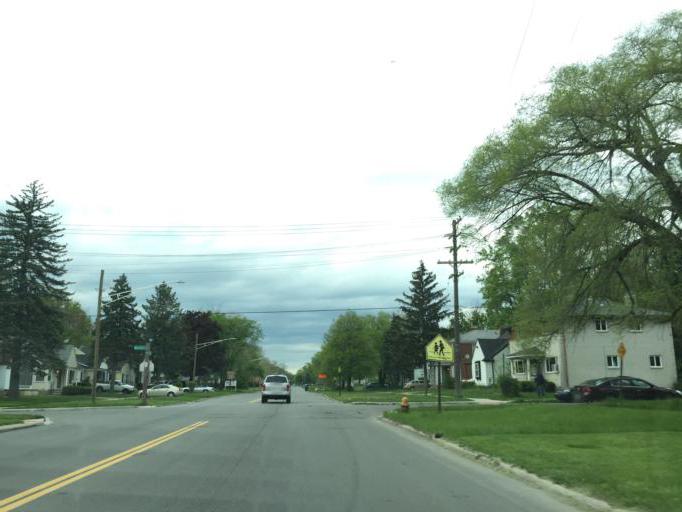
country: US
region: Michigan
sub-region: Wayne County
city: Redford
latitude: 42.3882
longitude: -83.2369
